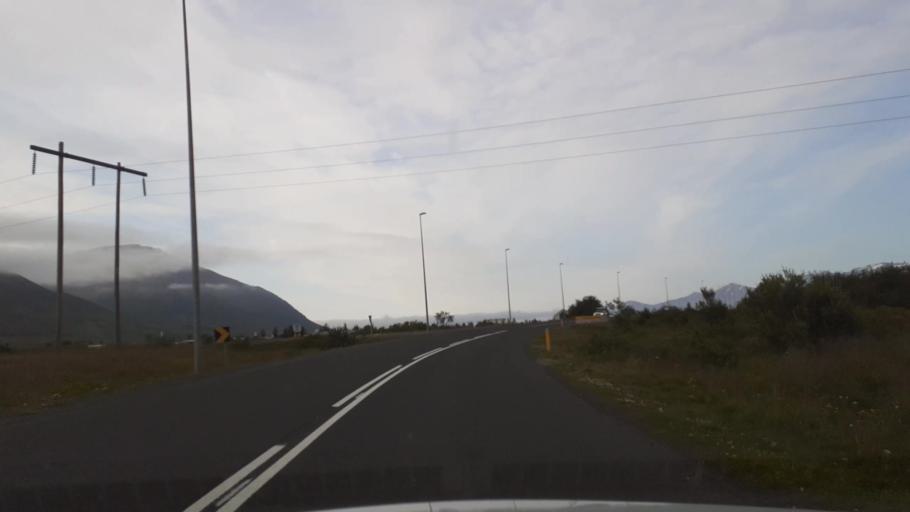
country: IS
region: Northeast
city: Dalvik
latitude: 65.9612
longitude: -18.5389
